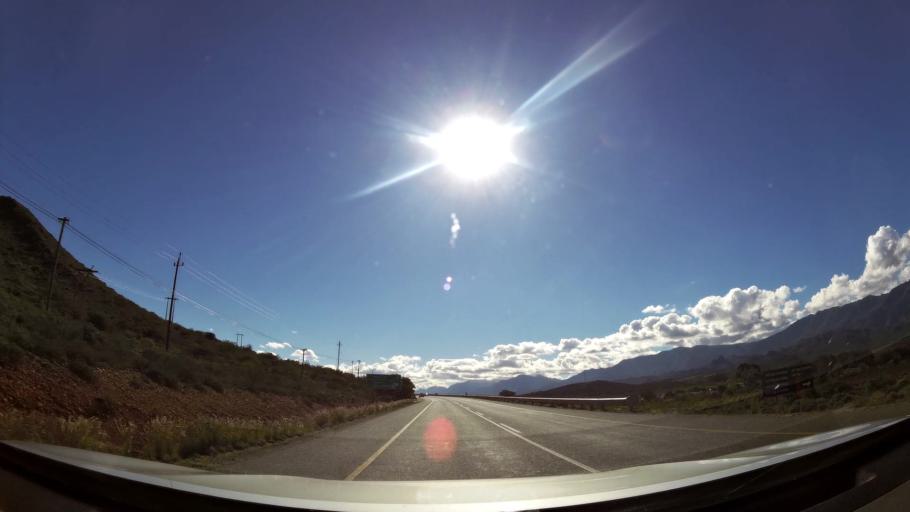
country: ZA
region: Western Cape
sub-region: Cape Winelands District Municipality
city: Ashton
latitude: -33.7803
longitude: 19.7663
